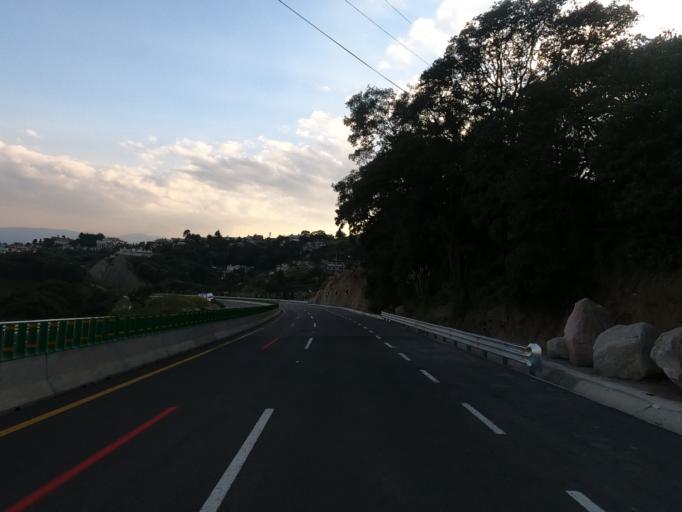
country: MX
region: Mexico
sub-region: Naucalpan de Juarez
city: Llano de las Flores (Barrio del Hueso)
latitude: 19.4285
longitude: -99.3323
